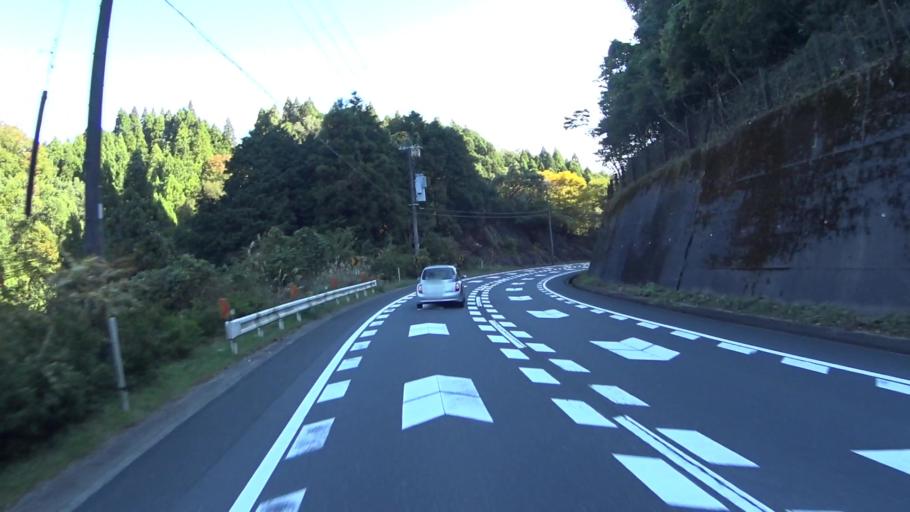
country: JP
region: Kyoto
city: Fukuchiyama
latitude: 35.3683
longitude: 135.1012
